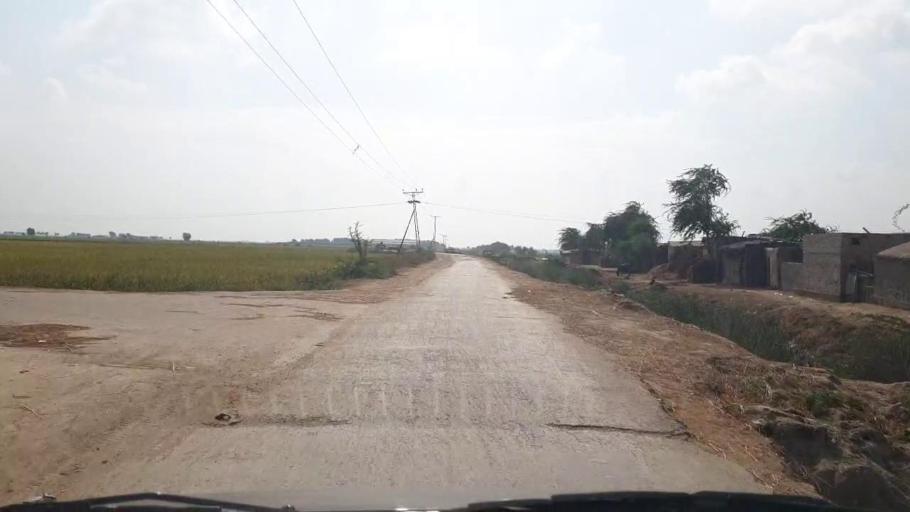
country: PK
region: Sindh
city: Kario
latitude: 24.6434
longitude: 68.5438
